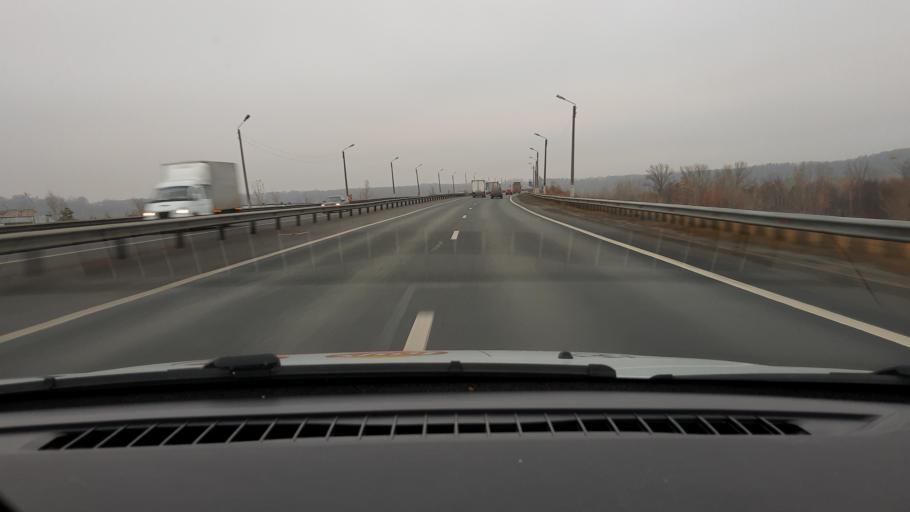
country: RU
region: Nizjnij Novgorod
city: Gorbatovka
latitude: 56.1978
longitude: 43.7517
